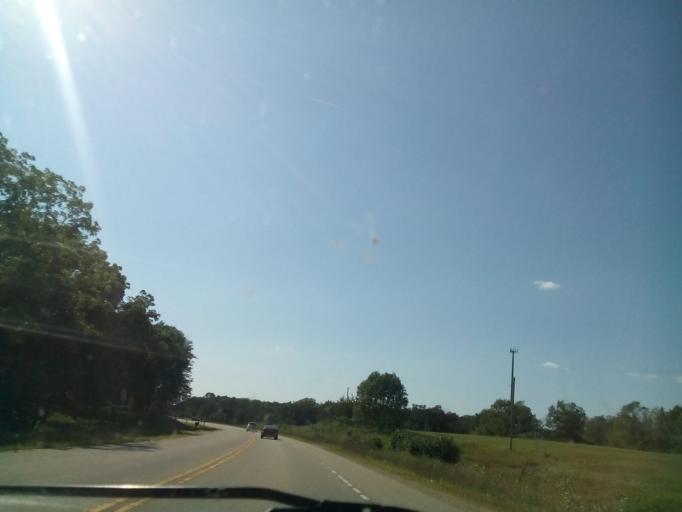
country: US
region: Wisconsin
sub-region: Dane County
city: Belleville
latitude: 42.8658
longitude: -89.5985
